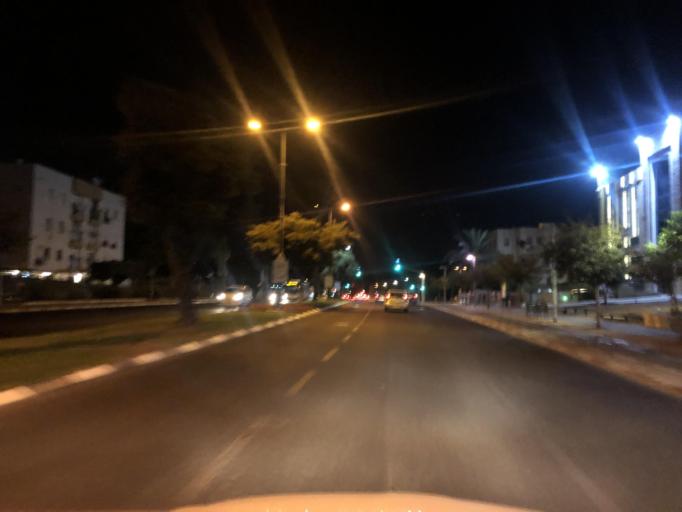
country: IL
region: Tel Aviv
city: Yafo
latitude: 32.0479
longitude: 34.7779
